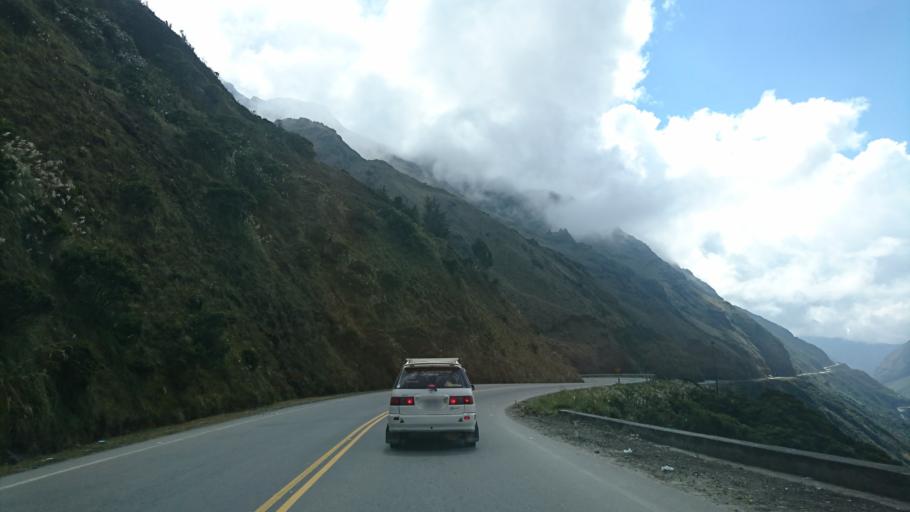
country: BO
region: La Paz
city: Coroico
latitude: -16.3170
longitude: -67.9270
